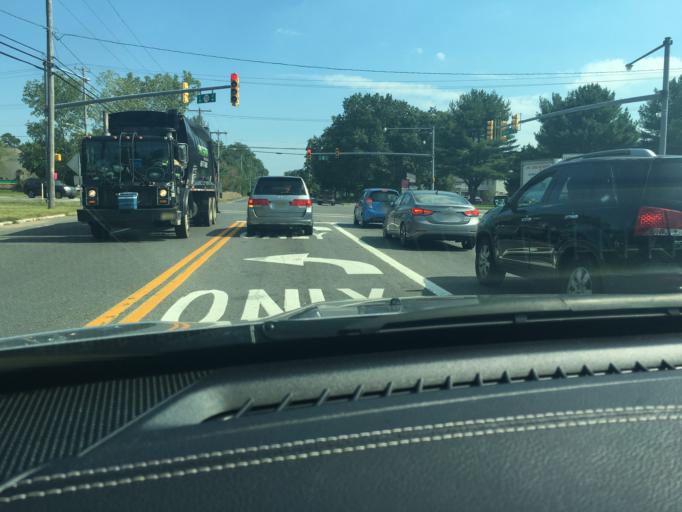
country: US
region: New Jersey
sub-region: Ocean County
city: Leisure Village West-Pine Lake Park
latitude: 40.0237
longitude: -74.2700
